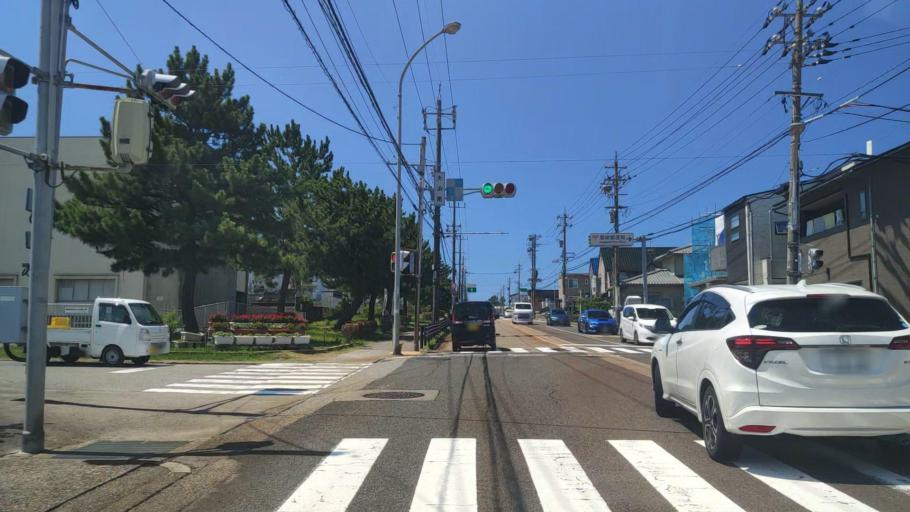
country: JP
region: Ishikawa
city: Kanazawa-shi
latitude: 36.6236
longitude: 136.6246
